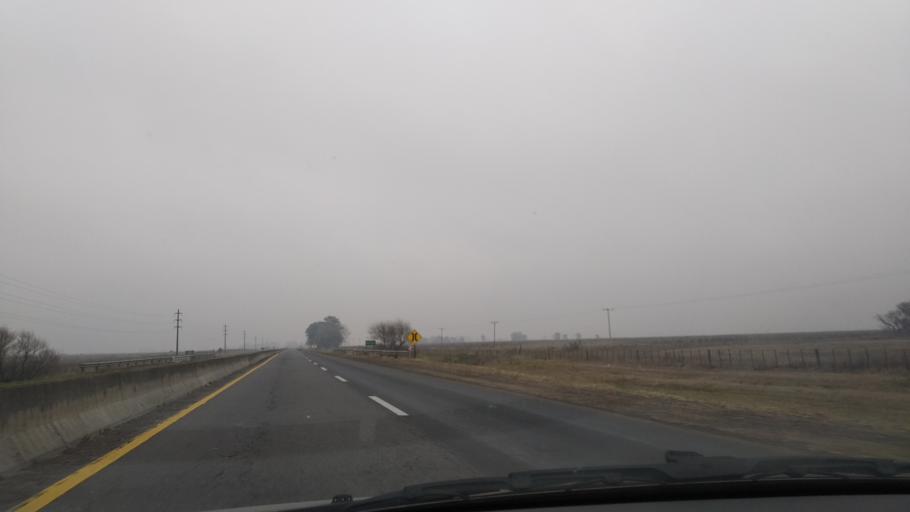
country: AR
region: Buenos Aires
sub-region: Partido de Azul
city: Azul
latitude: -36.8569
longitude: -60.0763
